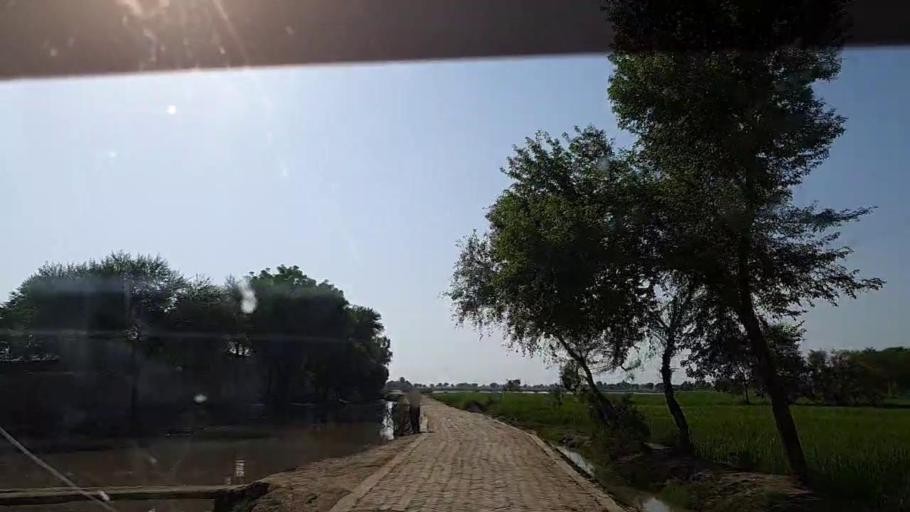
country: PK
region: Sindh
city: Tangwani
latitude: 28.2149
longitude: 68.9756
